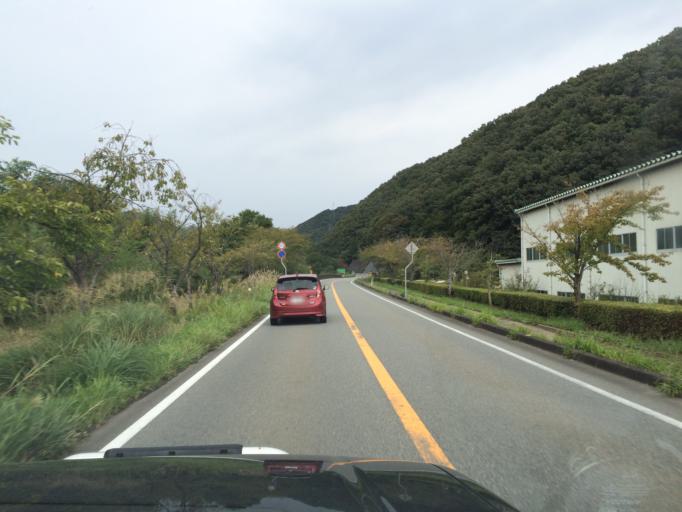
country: JP
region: Hyogo
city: Toyooka
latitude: 35.3602
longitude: 134.8289
